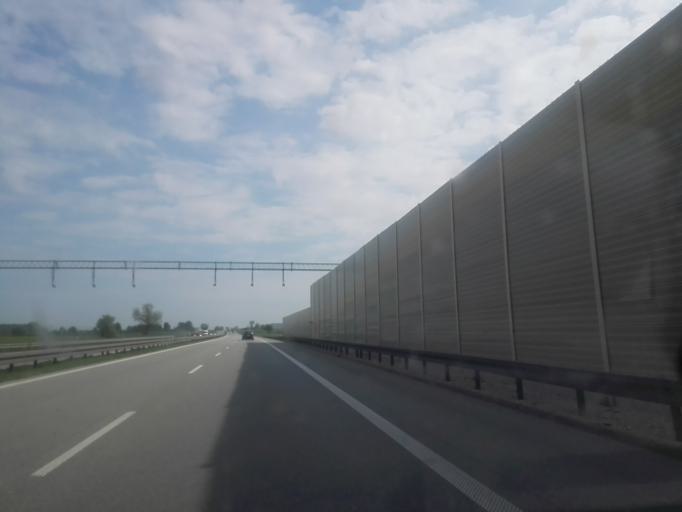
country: PL
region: Lodz Voivodeship
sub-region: Powiat rawski
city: Rawa Mazowiecka
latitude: 51.7892
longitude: 20.2856
